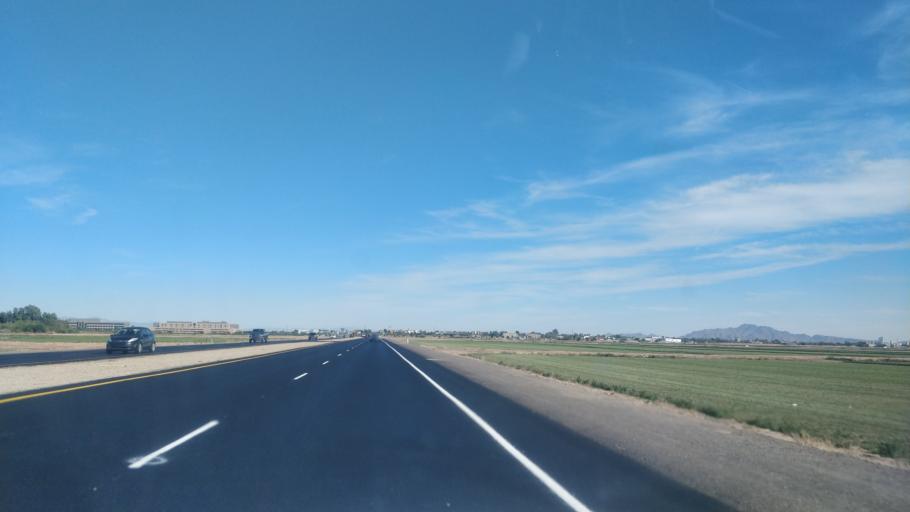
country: US
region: Arizona
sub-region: Maricopa County
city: Sun Lakes
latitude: 33.2609
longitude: -111.9067
